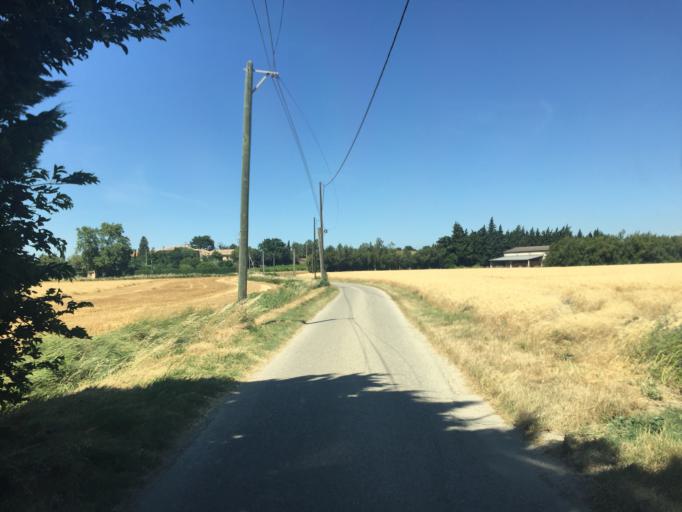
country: FR
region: Provence-Alpes-Cote d'Azur
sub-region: Departement du Vaucluse
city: Courthezon
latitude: 44.0751
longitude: 4.9170
